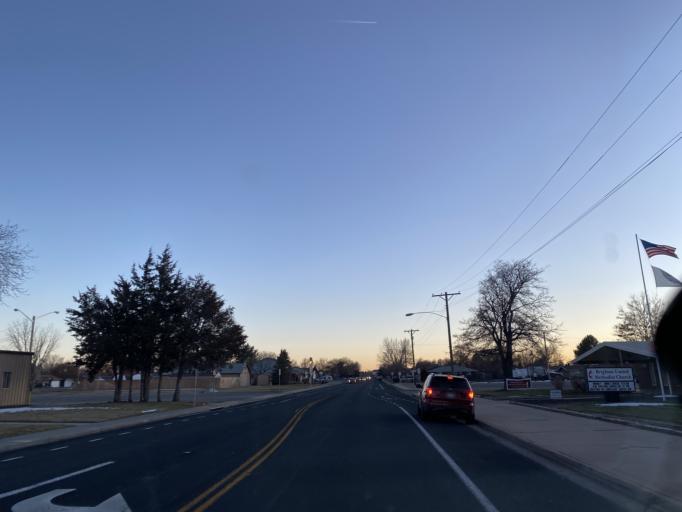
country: US
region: Colorado
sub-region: Adams County
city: Brighton
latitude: 39.9772
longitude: -104.8126
